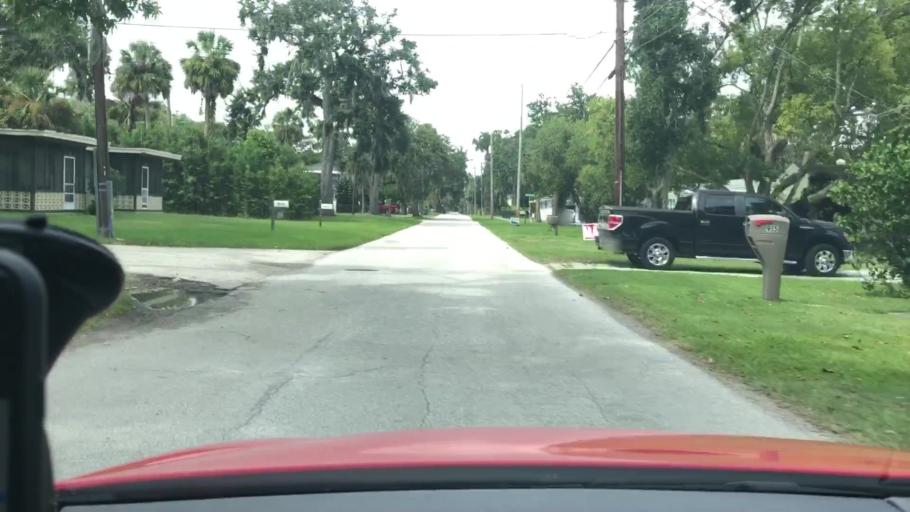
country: US
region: Florida
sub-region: Volusia County
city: Daytona Beach
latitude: 29.1953
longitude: -81.0131
